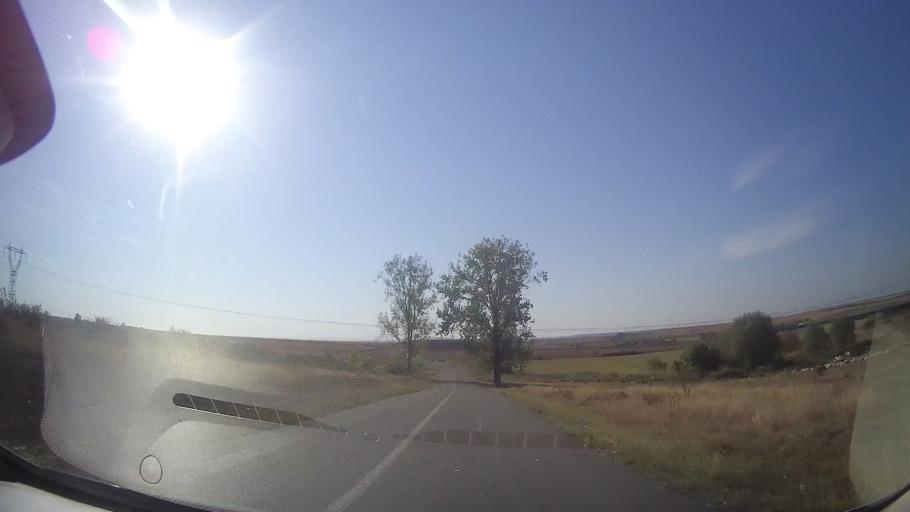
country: RO
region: Timis
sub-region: Comuna Topolovatu Mare
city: Topolovatu Mare
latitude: 45.8092
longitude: 21.5839
